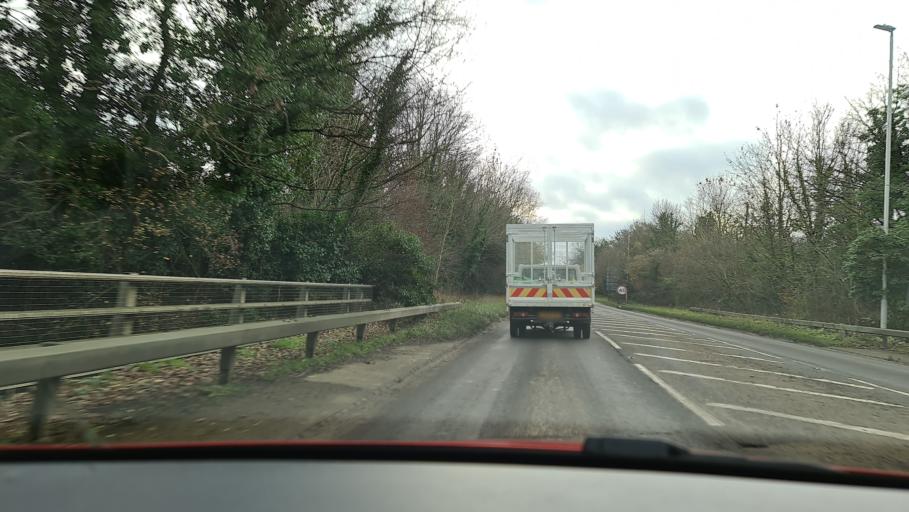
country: GB
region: England
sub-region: Buckinghamshire
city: Great Missenden
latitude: 51.7032
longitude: -0.7017
